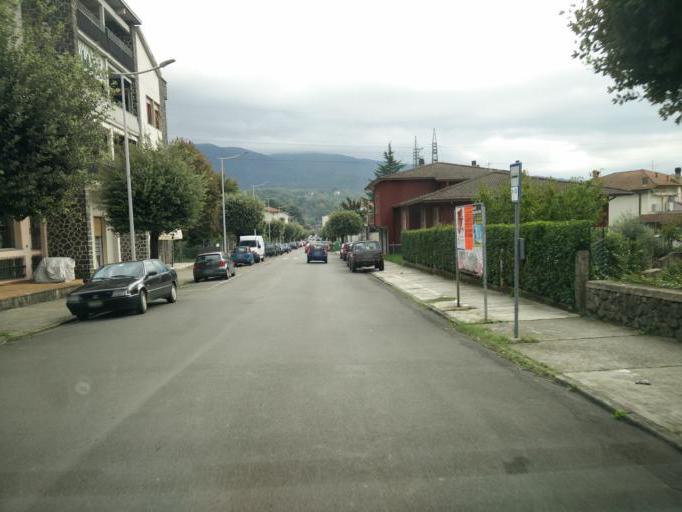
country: IT
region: Tuscany
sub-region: Provincia di Massa-Carrara
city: Pontremoli
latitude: 44.3749
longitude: 9.8746
